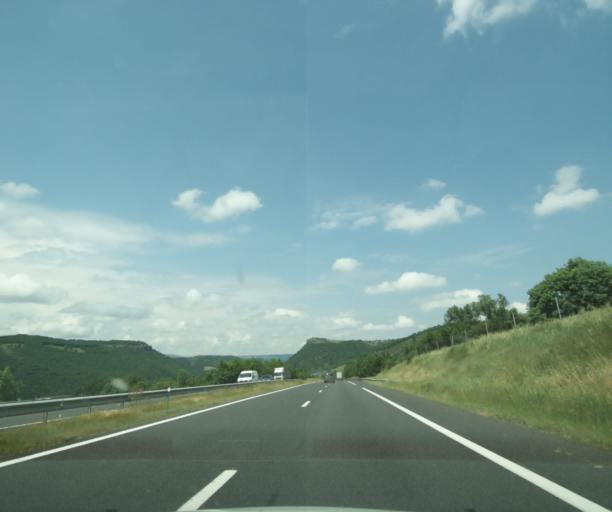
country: FR
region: Auvergne
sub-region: Departement du Cantal
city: Massiac
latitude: 45.2545
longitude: 3.2037
